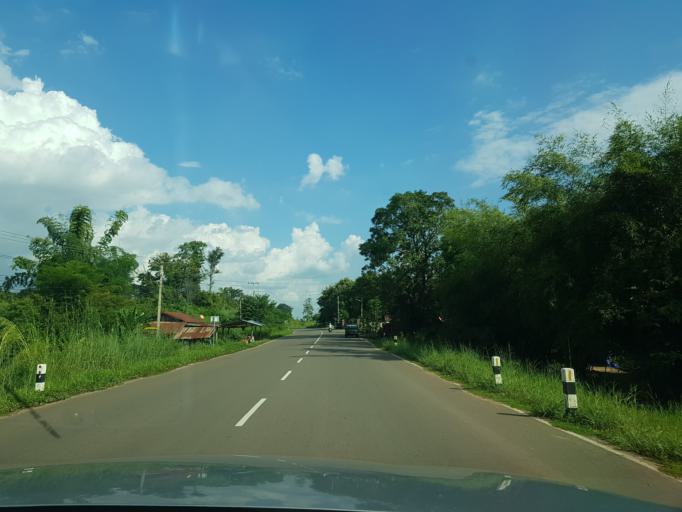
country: TH
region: Nong Khai
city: Pho Tak
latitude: 17.9864
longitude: 102.4380
